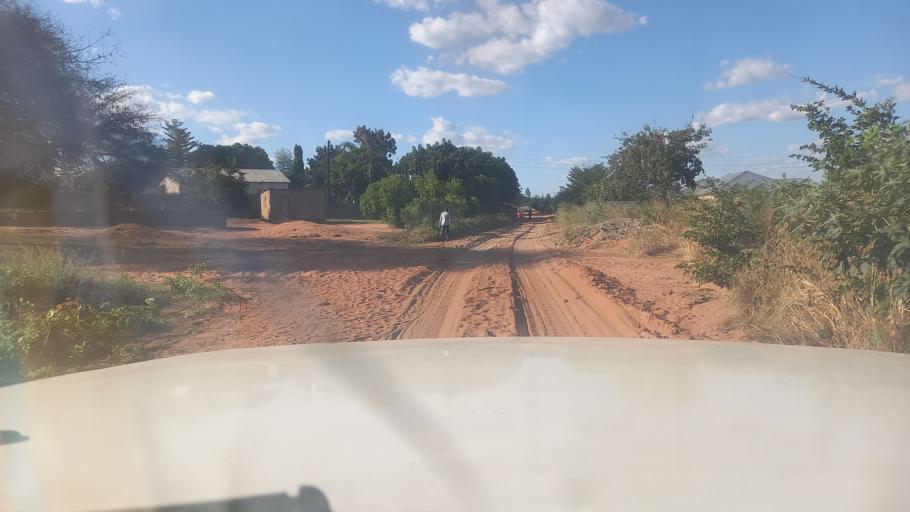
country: ZM
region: Southern
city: Livingstone
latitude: -17.8279
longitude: 25.8693
